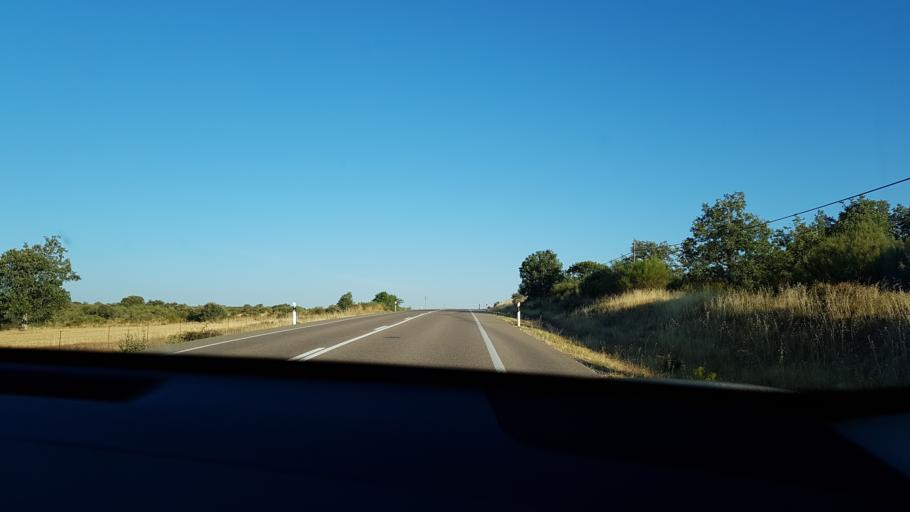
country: ES
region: Castille and Leon
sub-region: Provincia de Zamora
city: Samir de los Canos
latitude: 41.6506
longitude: -6.1722
